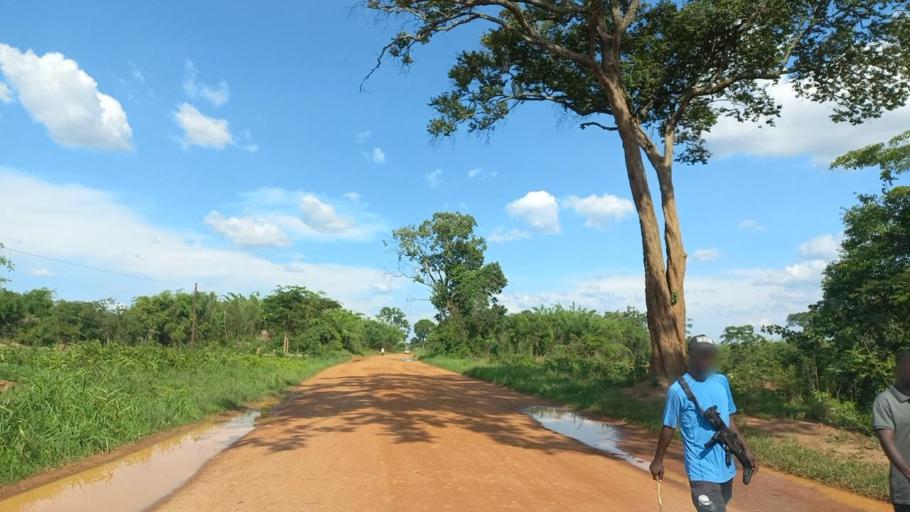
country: ZM
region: Copperbelt
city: Kitwe
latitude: -12.8644
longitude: 28.3758
